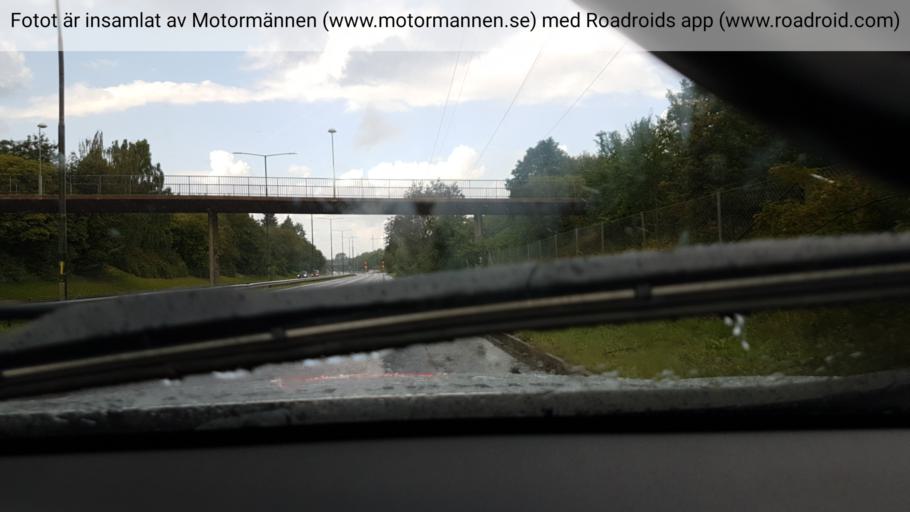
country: SE
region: Stockholm
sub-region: Stockholms Kommun
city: Arsta
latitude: 59.2668
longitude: 18.0604
